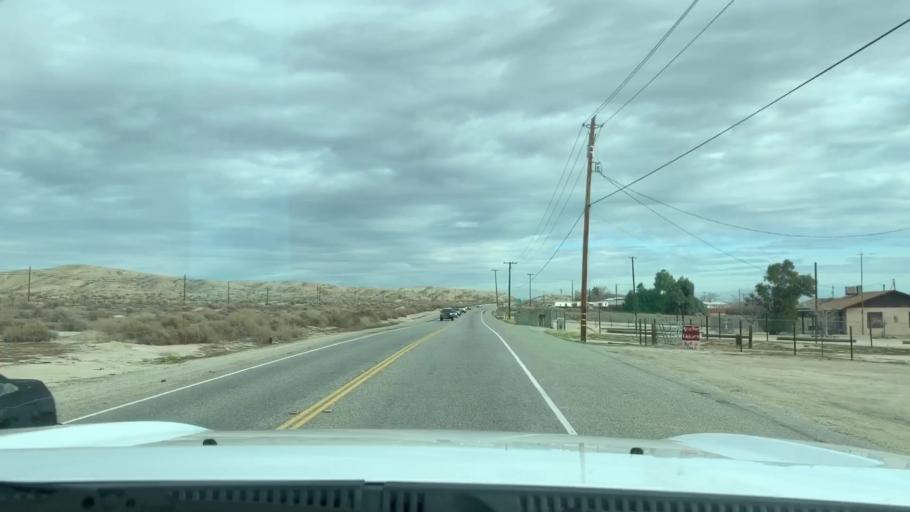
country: US
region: California
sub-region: Kern County
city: Ford City
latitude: 35.2305
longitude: -119.3740
